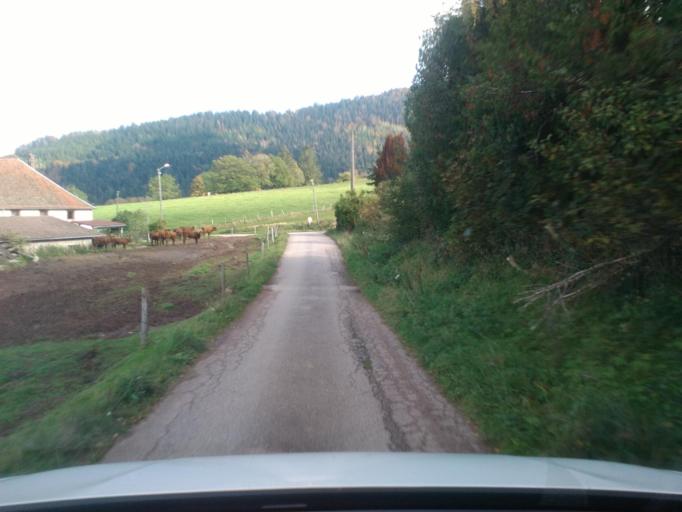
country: FR
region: Lorraine
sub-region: Departement des Vosges
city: Senones
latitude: 48.4004
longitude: 7.0732
